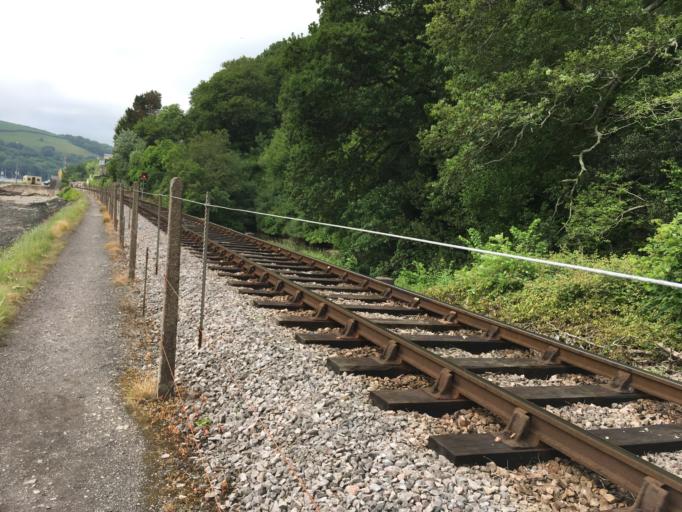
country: GB
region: England
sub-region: Devon
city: Dartmouth
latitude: 50.3586
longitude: -3.5718
